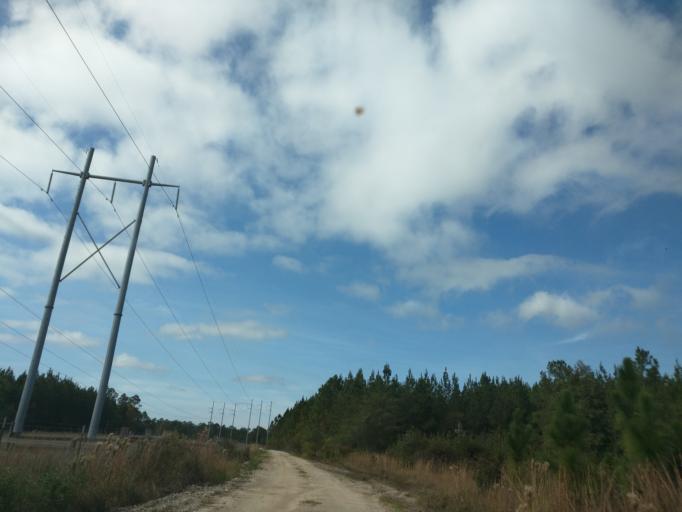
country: US
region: Florida
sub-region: Escambia County
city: Cantonment
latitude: 30.5324
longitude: -87.4331
